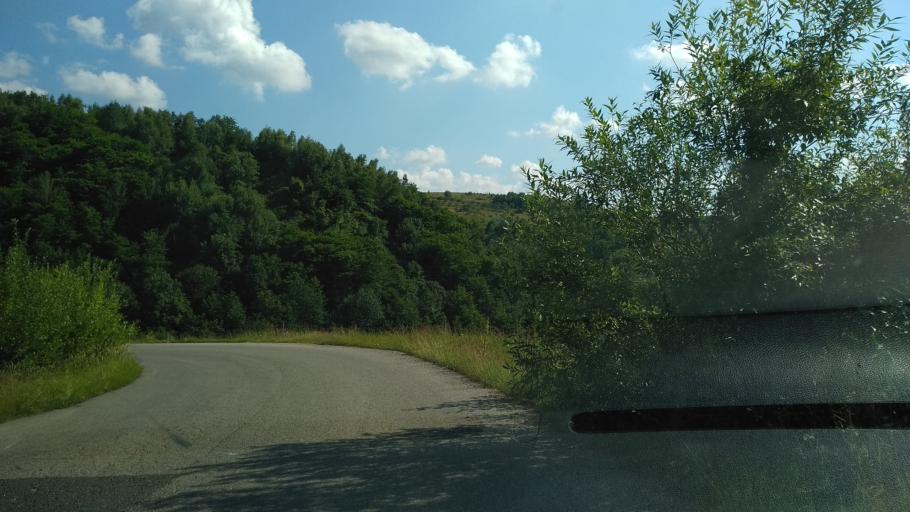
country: RO
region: Hunedoara
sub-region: Comuna Orastioara de Sus
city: Orastioara de Sus
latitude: 45.7074
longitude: 23.1410
